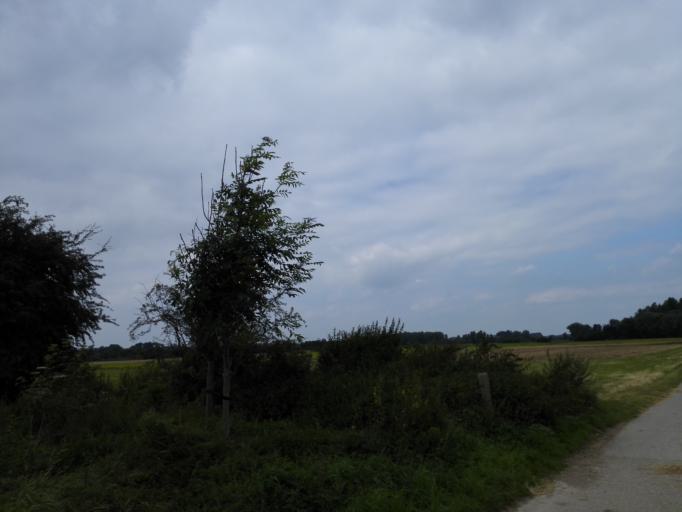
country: BE
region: Flanders
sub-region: Provincie Vlaams-Brabant
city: Tienen
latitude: 50.8066
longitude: 4.9878
